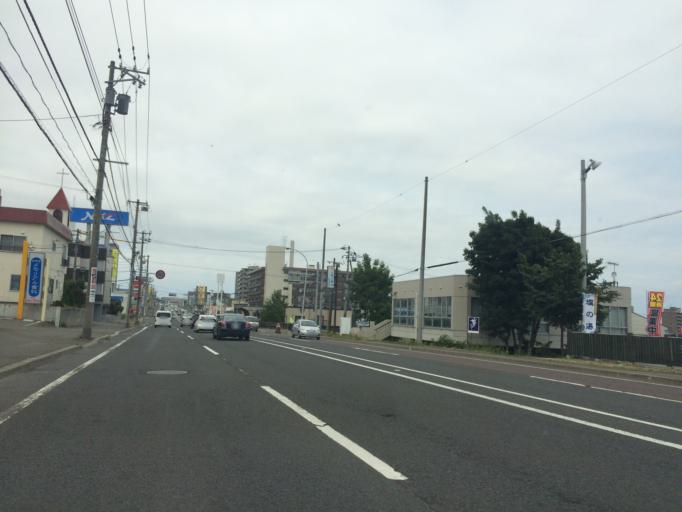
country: JP
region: Hokkaido
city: Sapporo
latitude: 43.1045
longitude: 141.2515
